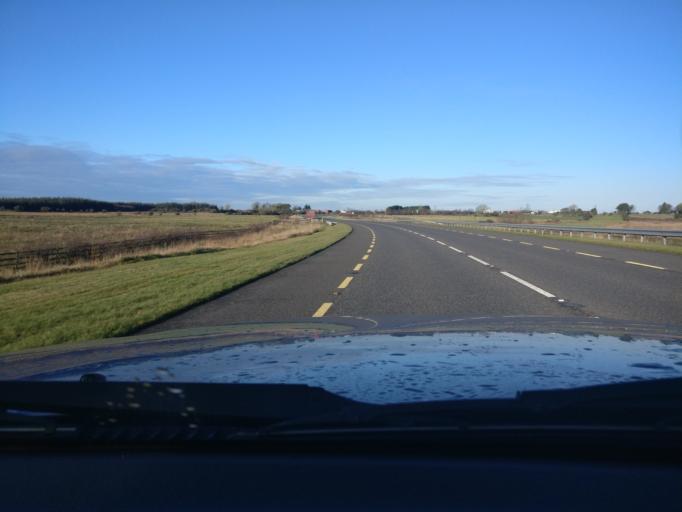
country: IE
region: Connaught
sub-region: County Galway
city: Loughrea
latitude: 53.2557
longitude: -8.5985
